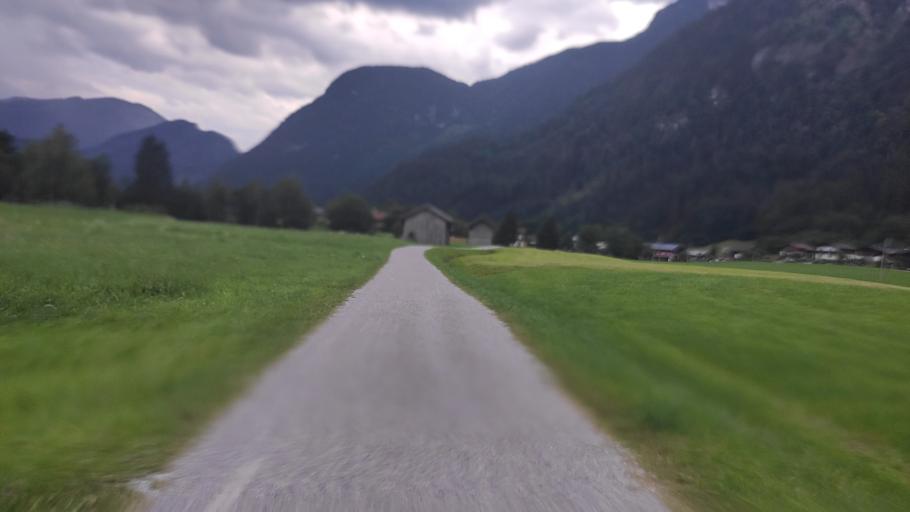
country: AT
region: Salzburg
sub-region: Politischer Bezirk Zell am See
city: Lofer
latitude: 47.5772
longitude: 12.6913
